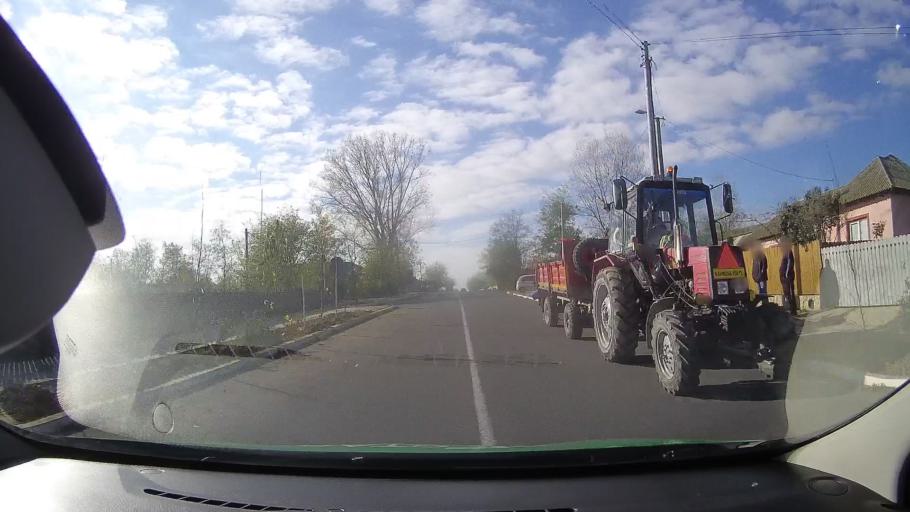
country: RO
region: Tulcea
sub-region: Comuna Mahmudia
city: Mahmudia
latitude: 45.0831
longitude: 29.0827
